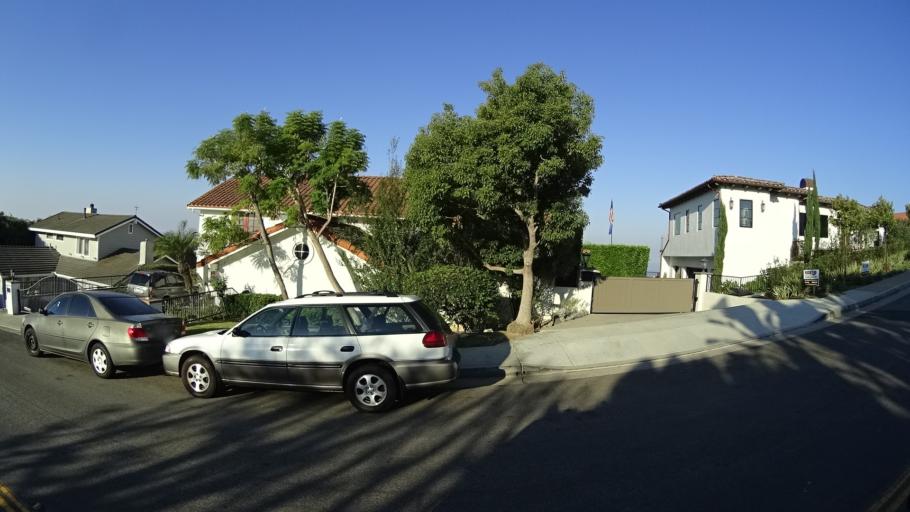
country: US
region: California
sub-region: Orange County
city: San Clemente
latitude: 33.4260
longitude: -117.6004
